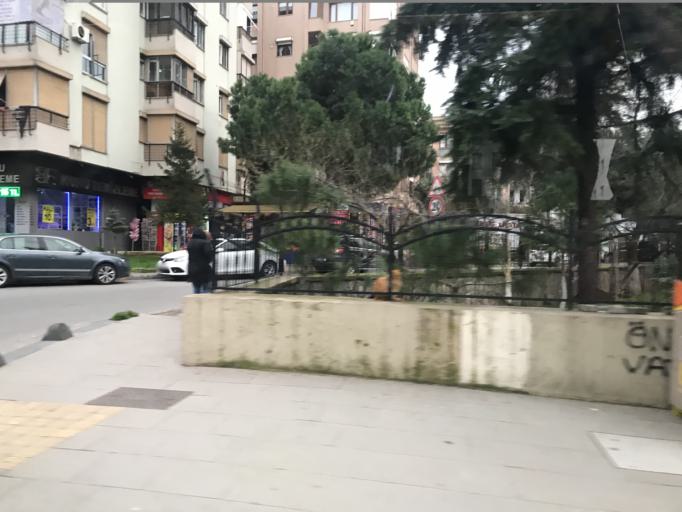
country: TR
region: Istanbul
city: UEskuedar
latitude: 40.9835
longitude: 29.0614
